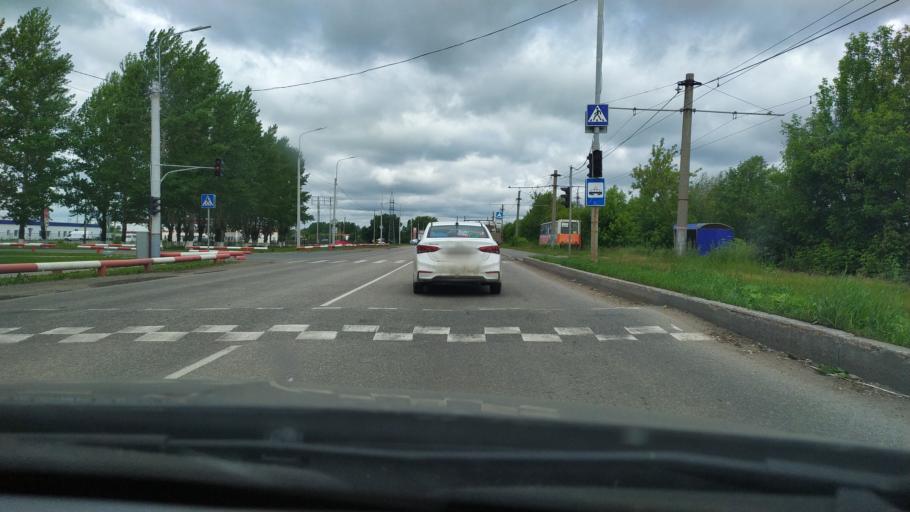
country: RU
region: Perm
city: Kondratovo
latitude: 57.9292
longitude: 56.1307
